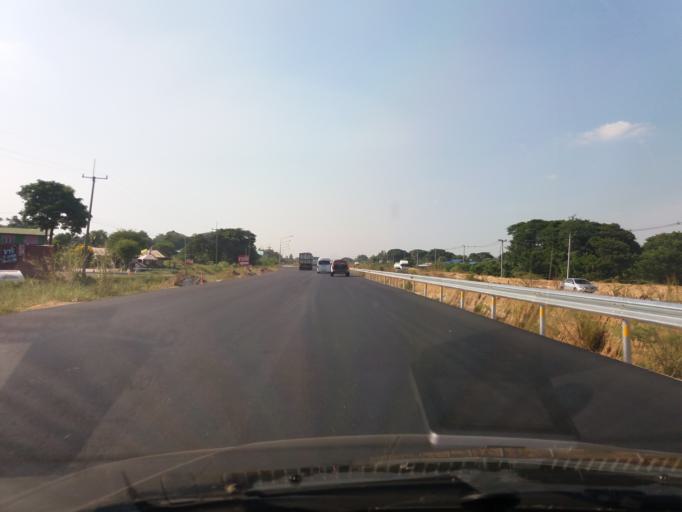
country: TH
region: Nakhon Sawan
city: Krok Phra
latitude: 15.6275
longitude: 100.1078
